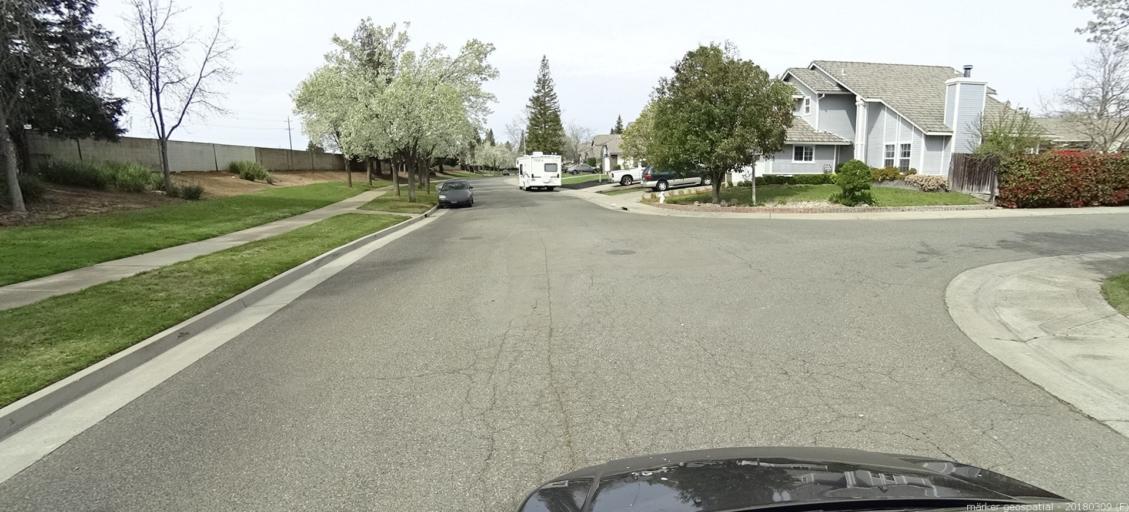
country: US
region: California
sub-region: Sacramento County
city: Vineyard
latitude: 38.4570
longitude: -121.3819
